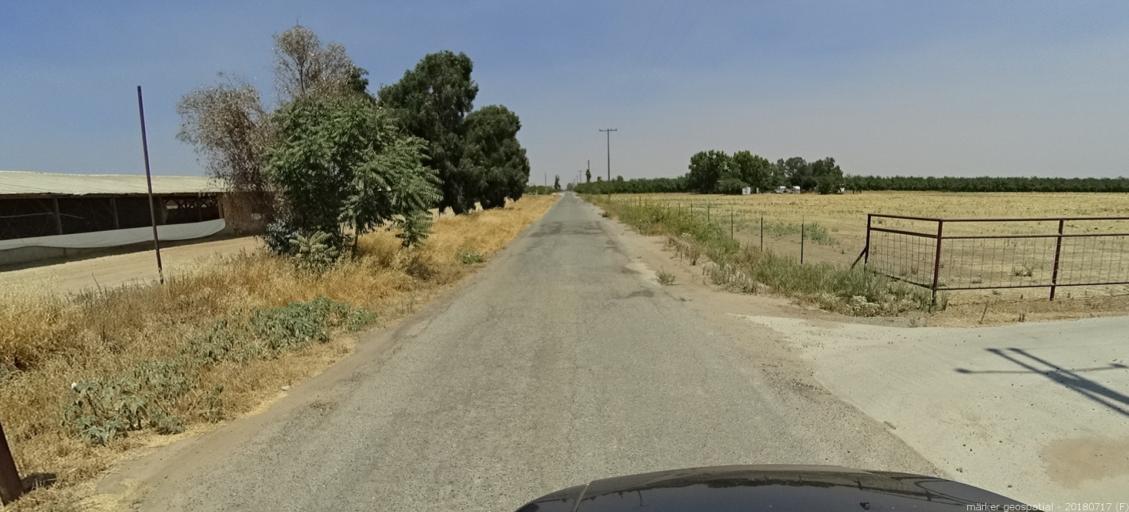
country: US
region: California
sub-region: Madera County
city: Fairmead
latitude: 37.1287
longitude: -120.1292
